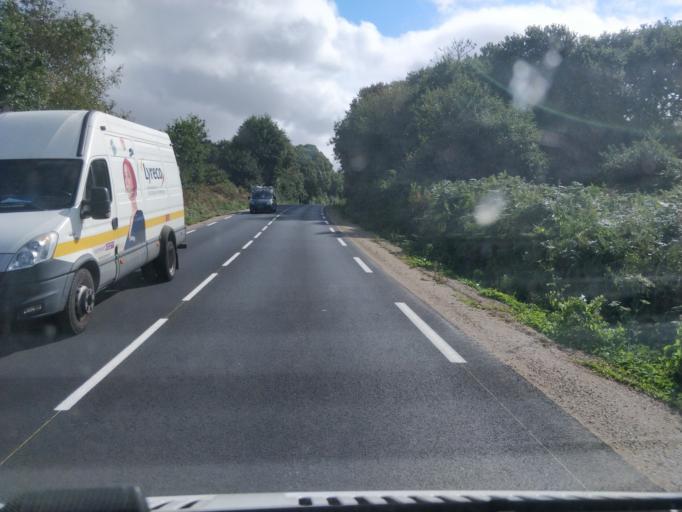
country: FR
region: Brittany
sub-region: Departement du Finistere
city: Landudec
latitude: 47.9999
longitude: -4.3236
